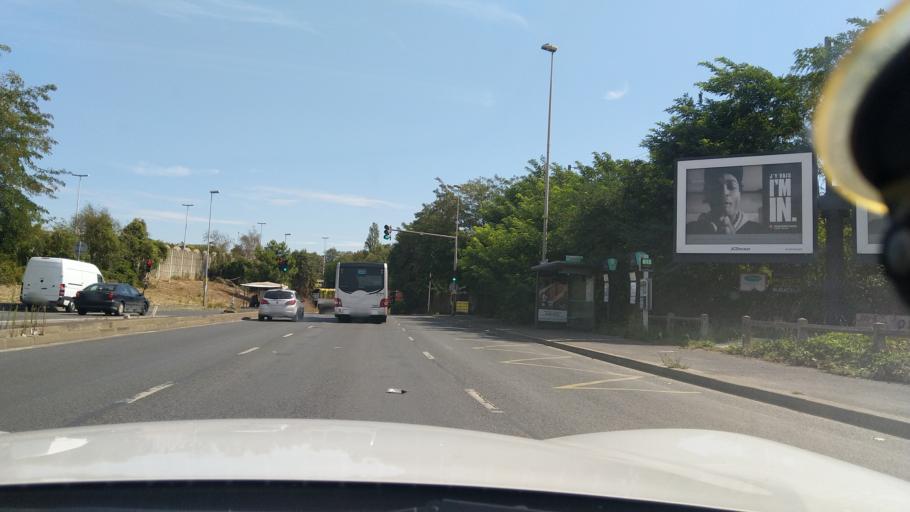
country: FR
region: Ile-de-France
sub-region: Departement de Seine-Saint-Denis
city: Bobigny
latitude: 48.9056
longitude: 2.4610
